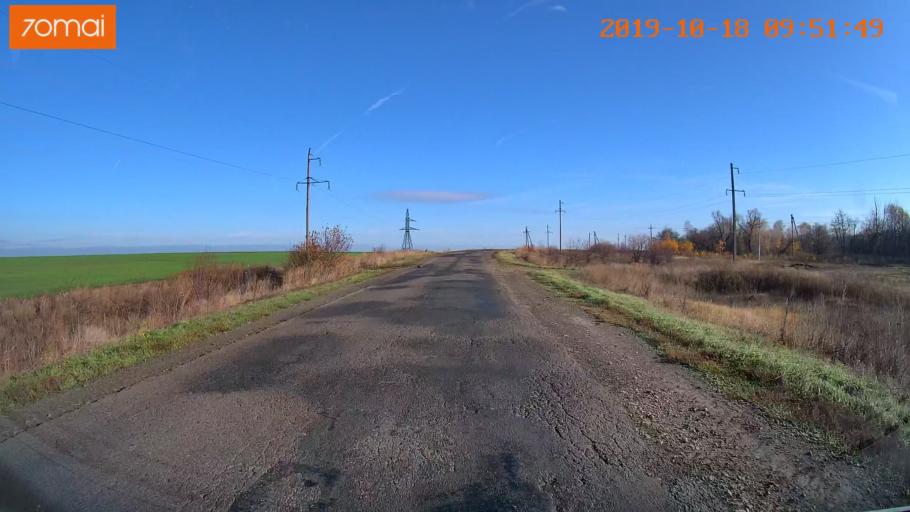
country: RU
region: Tula
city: Kazachka
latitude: 53.3453
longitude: 38.2985
